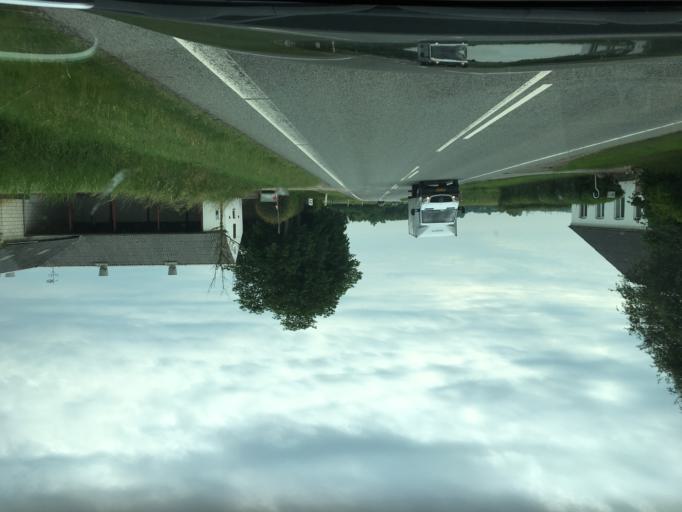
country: DK
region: South Denmark
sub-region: Kolding Kommune
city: Kolding
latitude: 55.5934
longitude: 9.4933
